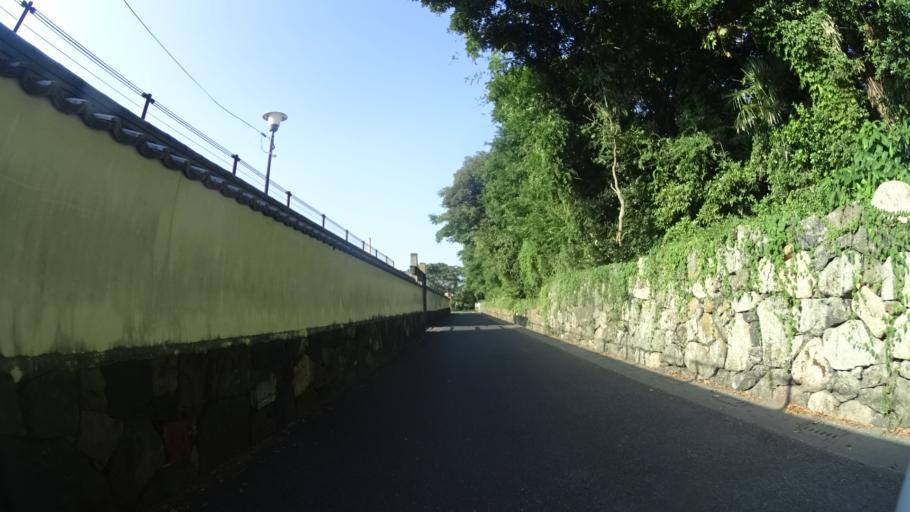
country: JP
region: Yamaguchi
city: Hagi
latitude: 34.4140
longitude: 131.3843
